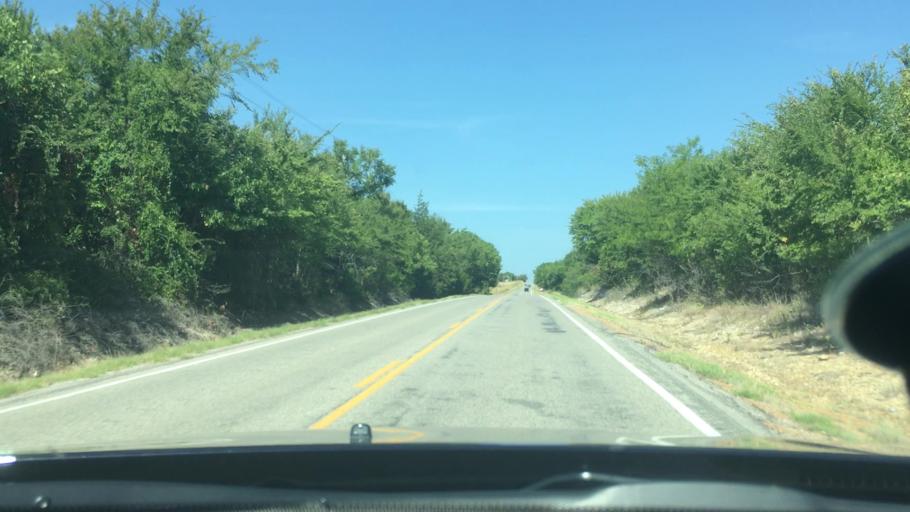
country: US
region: Oklahoma
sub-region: Marshall County
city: Oakland
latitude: 33.9983
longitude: -96.8350
